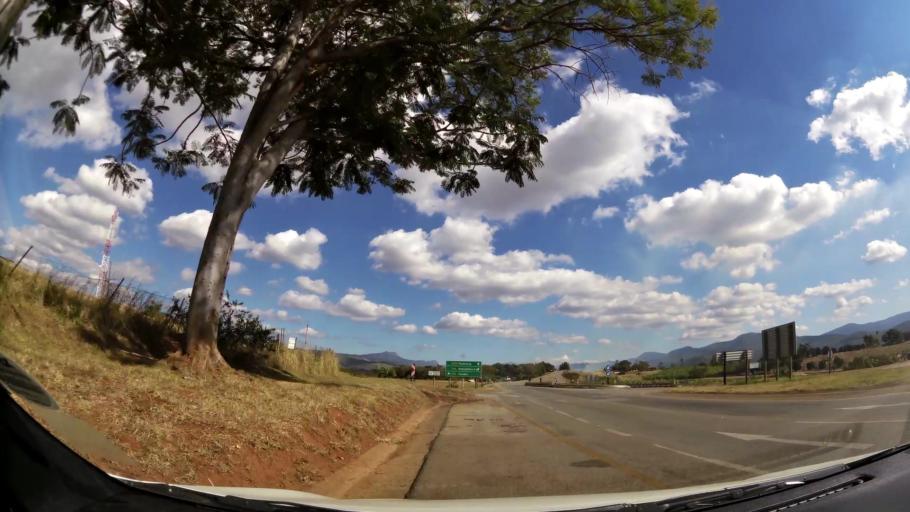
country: ZA
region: Limpopo
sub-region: Mopani District Municipality
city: Tzaneen
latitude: -23.8350
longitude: 30.1373
